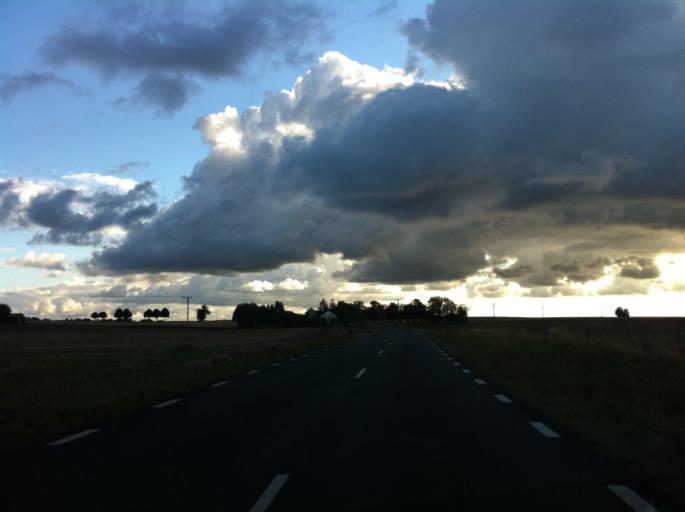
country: SE
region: Skane
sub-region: Svalovs Kommun
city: Svaloev
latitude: 55.9041
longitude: 13.1942
